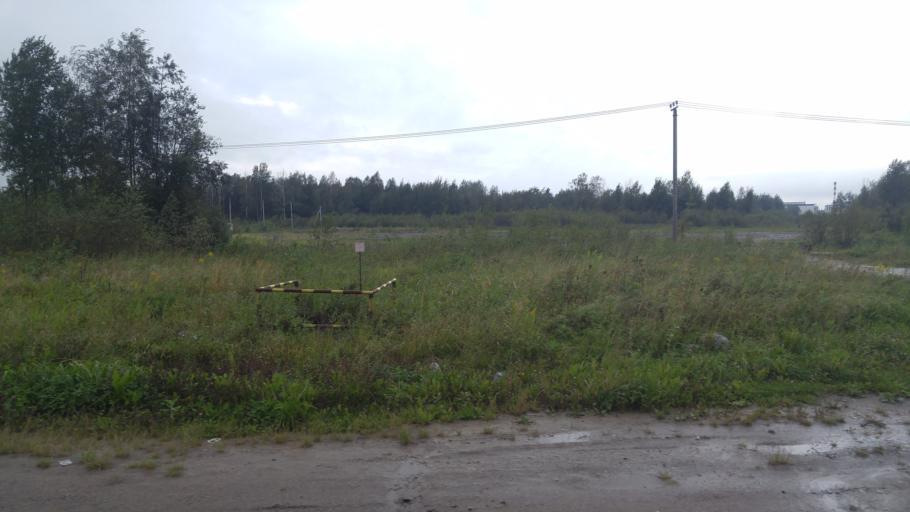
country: RU
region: St.-Petersburg
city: Ust'-Izhora
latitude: 59.7834
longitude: 30.5735
